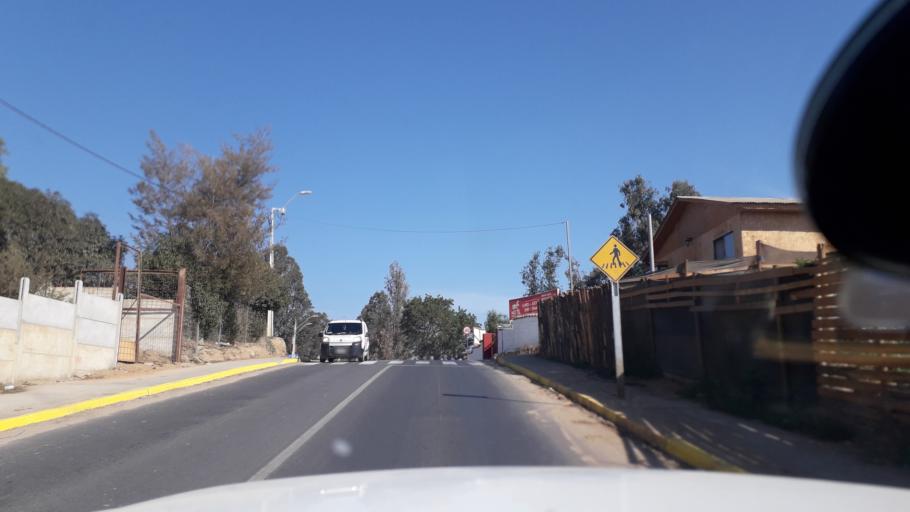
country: CL
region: Valparaiso
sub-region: Provincia de Marga Marga
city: Villa Alemana
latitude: -33.0712
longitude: -71.4047
